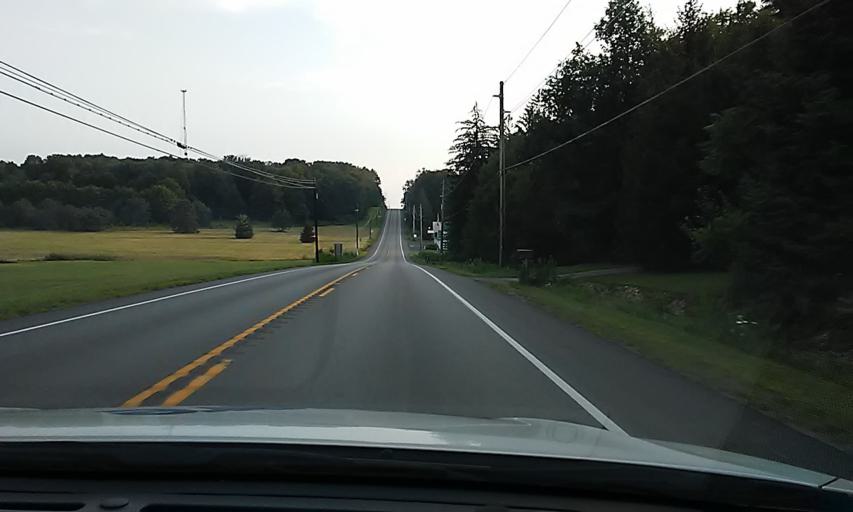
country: US
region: Pennsylvania
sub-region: Forest County
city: Marienville
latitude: 41.4761
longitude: -79.1143
